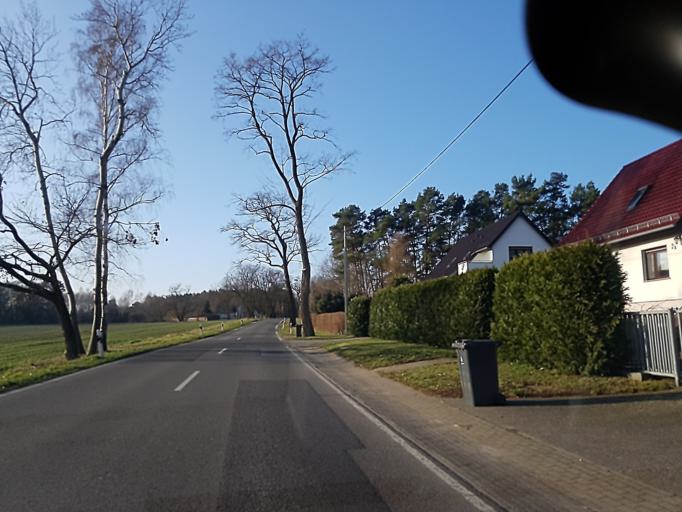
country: DE
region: Brandenburg
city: Bad Liebenwerda
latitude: 51.5278
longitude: 13.4179
